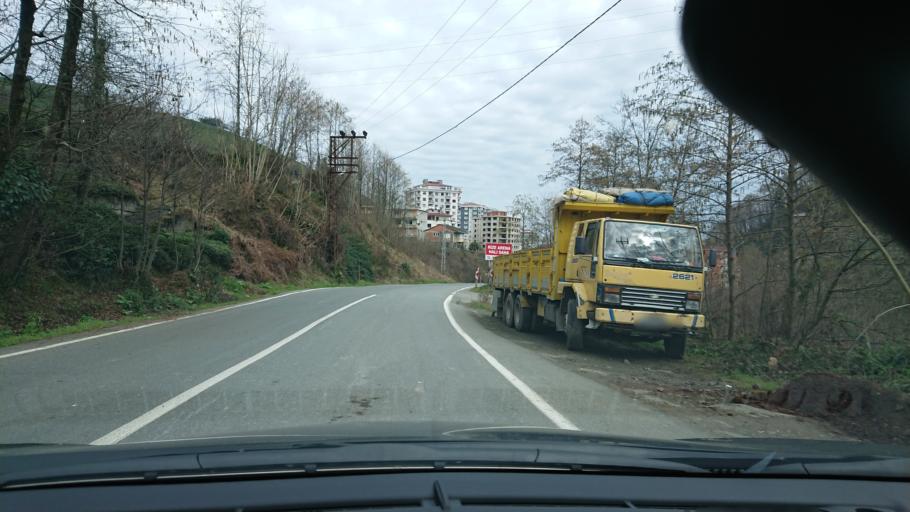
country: TR
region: Rize
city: Rize
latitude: 41.0269
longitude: 40.5058
